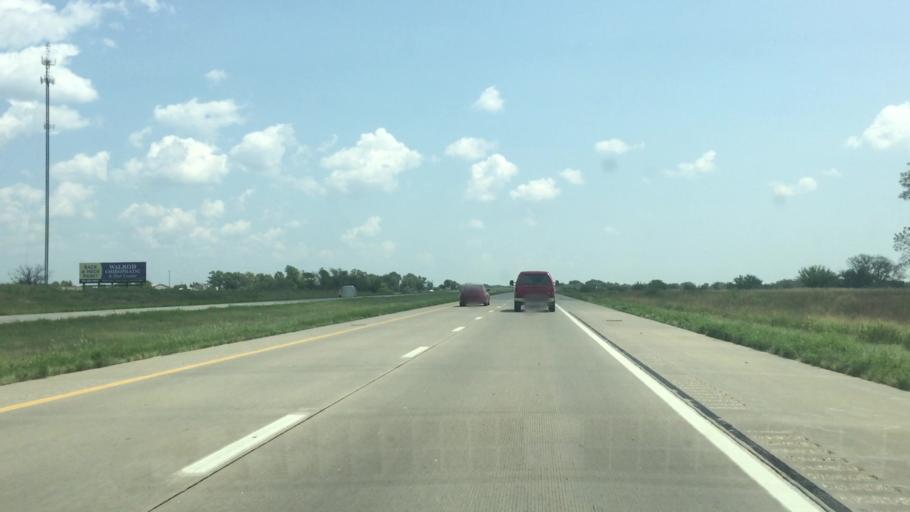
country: US
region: Kansas
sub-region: Franklin County
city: Wellsville
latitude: 38.6898
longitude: -95.1127
